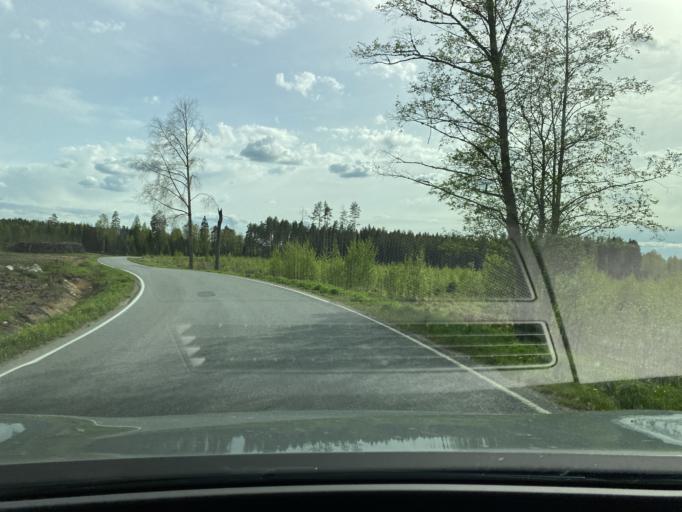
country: FI
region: Varsinais-Suomi
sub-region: Salo
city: Kiikala
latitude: 60.5201
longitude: 23.5394
